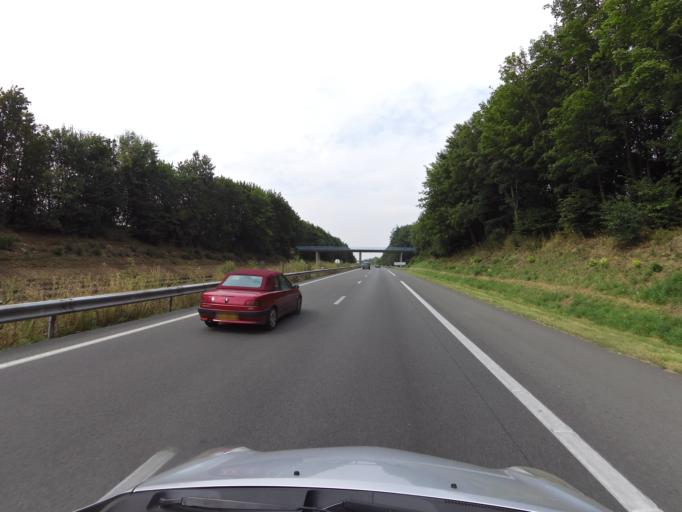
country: FR
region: Nord-Pas-de-Calais
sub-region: Departement du Nord
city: Gouzeaucourt
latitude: 50.0584
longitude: 3.1785
